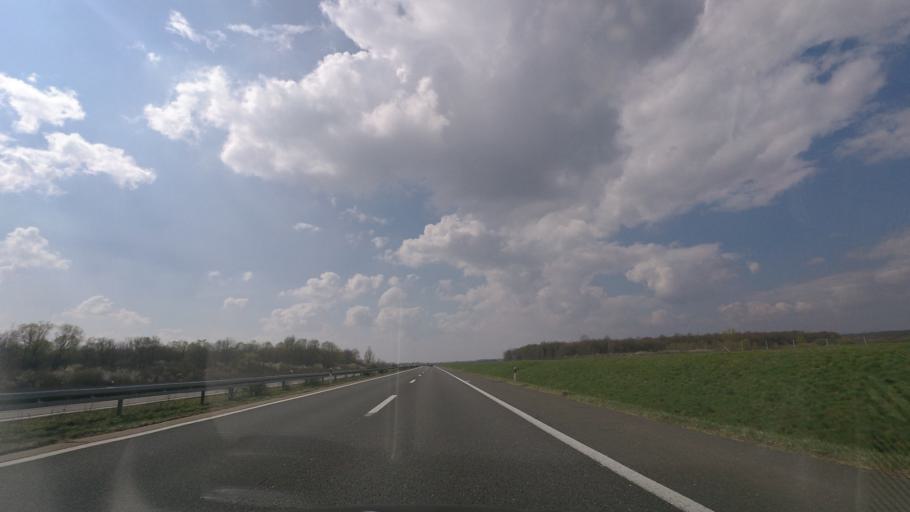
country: HR
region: Zagrebacka
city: Jastrebarsko
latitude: 45.6192
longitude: 15.6485
